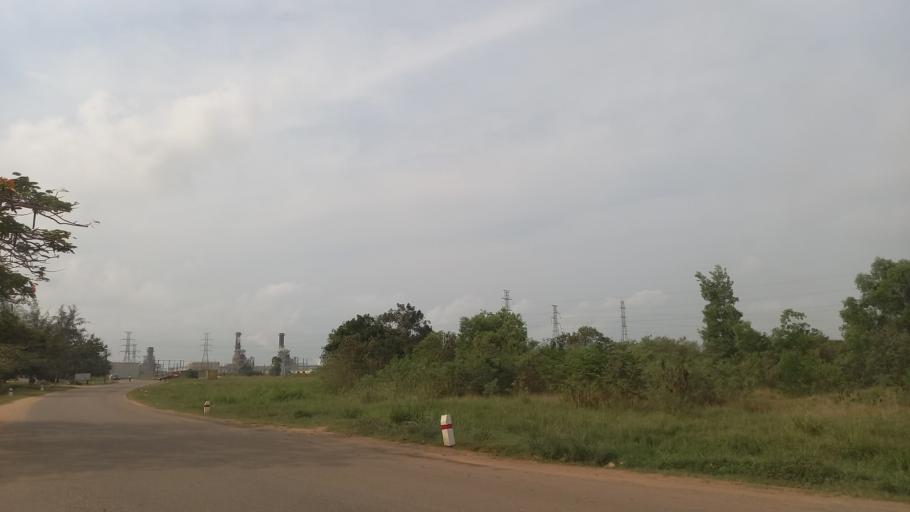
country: GH
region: Western
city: Shama Junction
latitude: 4.9792
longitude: -1.6588
